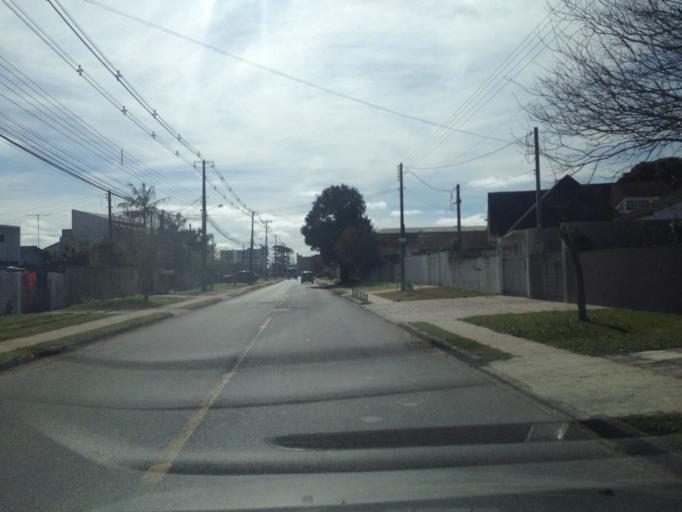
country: BR
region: Parana
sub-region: Sao Jose Dos Pinhais
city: Sao Jose dos Pinhais
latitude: -25.5602
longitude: -49.1712
